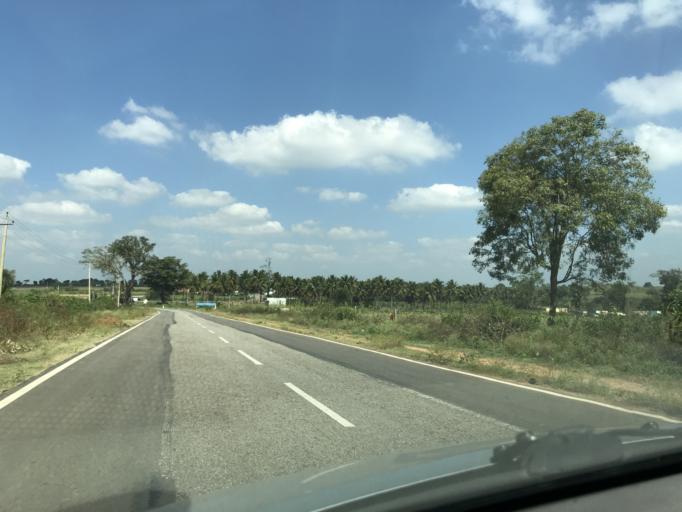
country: IN
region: Karnataka
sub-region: Mysore
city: Heggadadevankote
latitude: 12.1642
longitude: 76.2792
